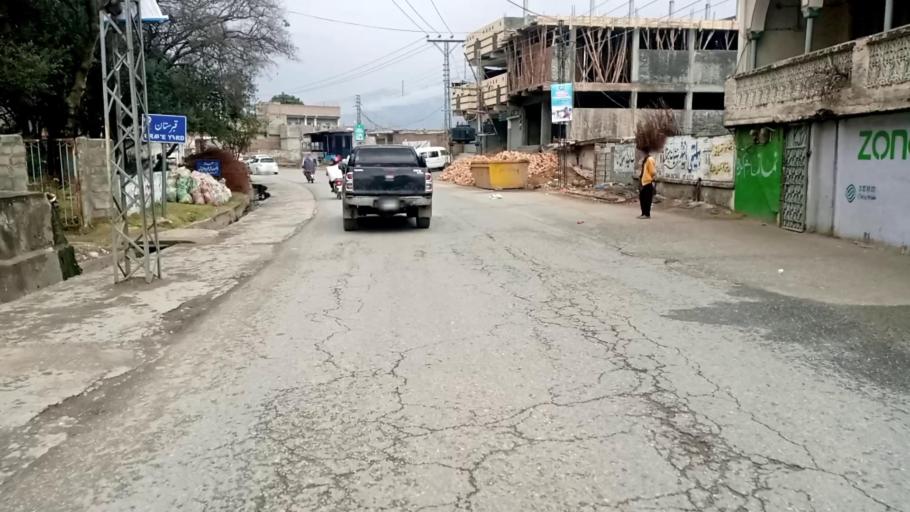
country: PK
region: Khyber Pakhtunkhwa
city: Mingora
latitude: 34.8412
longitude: 72.4161
